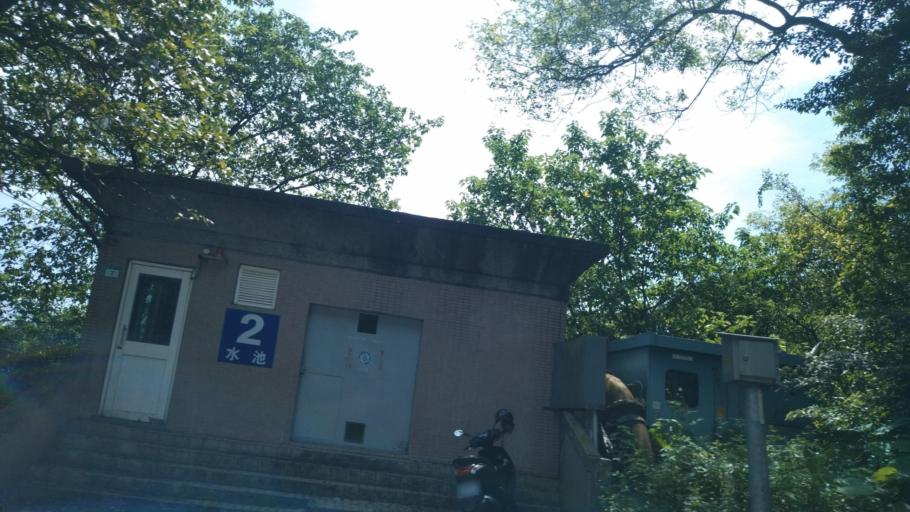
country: TW
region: Taipei
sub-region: Taipei
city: Banqiao
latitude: 24.9446
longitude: 121.5044
